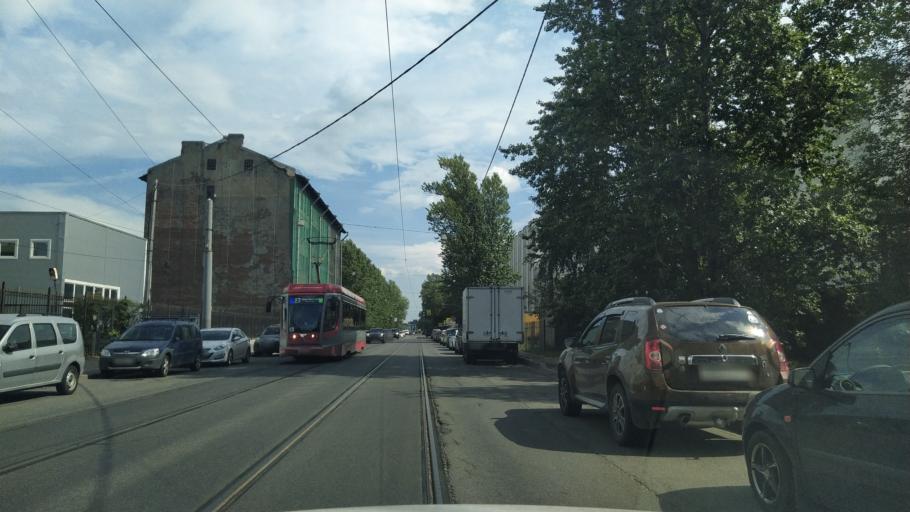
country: RU
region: Leningrad
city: Finlyandskiy
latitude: 59.9660
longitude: 30.3895
